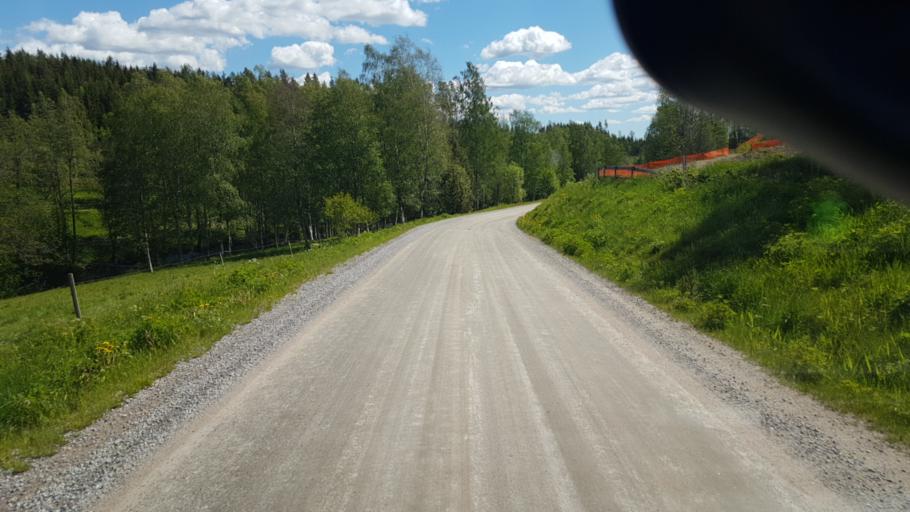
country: SE
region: Vaermland
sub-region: Sunne Kommun
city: Sunne
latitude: 59.6825
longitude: 12.8950
